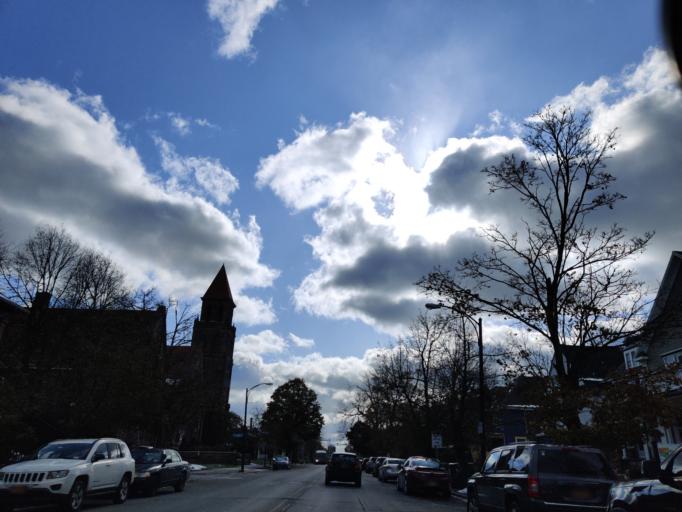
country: US
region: New York
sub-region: Erie County
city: Buffalo
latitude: 42.9217
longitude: -78.8770
